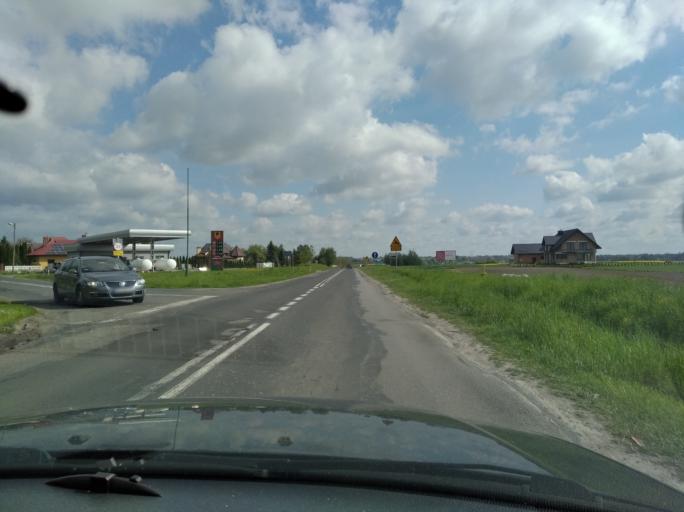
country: PL
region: Subcarpathian Voivodeship
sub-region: Powiat przeworski
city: Urzejowice
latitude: 50.0359
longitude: 22.4709
